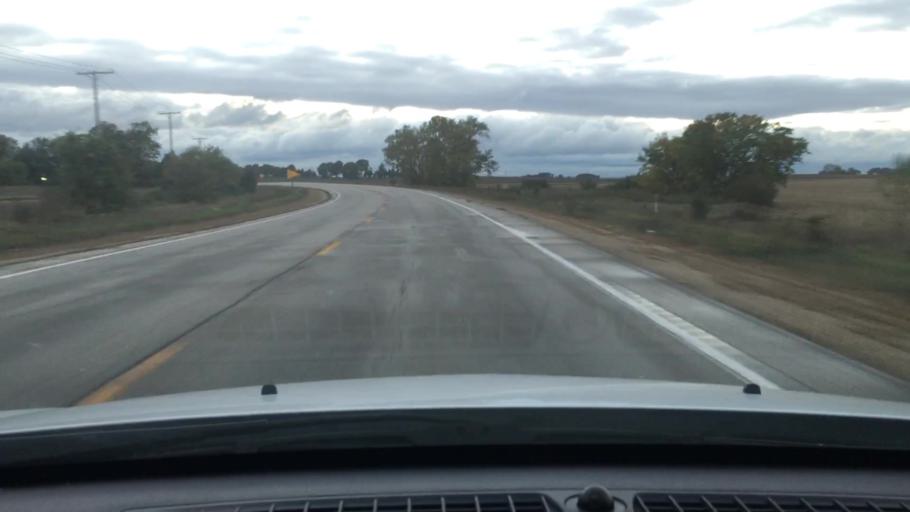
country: US
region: Illinois
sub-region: DeKalb County
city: Malta
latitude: 41.9355
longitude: -88.8066
